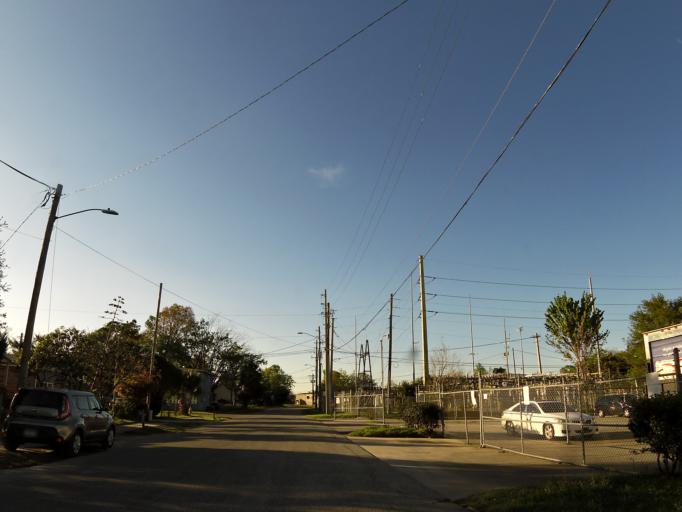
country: US
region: Florida
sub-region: Duval County
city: Jacksonville
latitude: 30.3355
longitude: -81.6893
